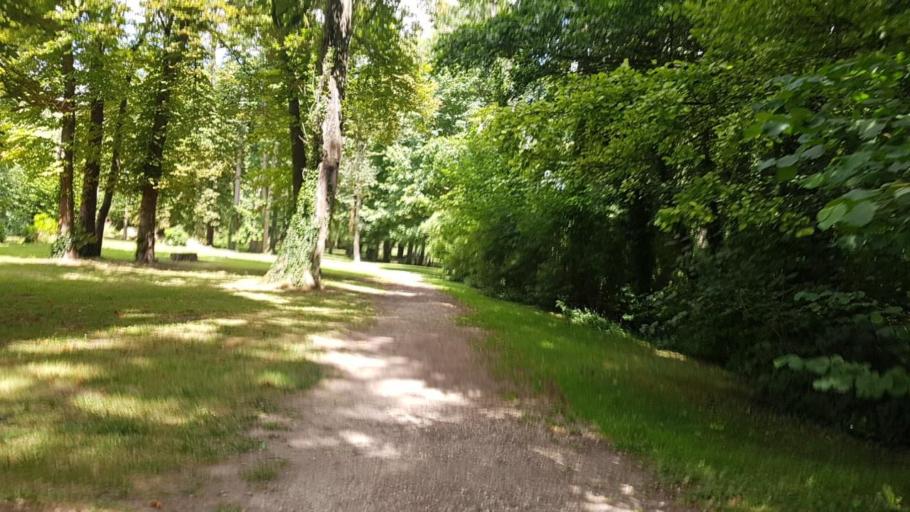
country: FR
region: Ile-de-France
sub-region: Departement de Seine-et-Marne
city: Claye-Souilly
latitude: 48.9612
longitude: 2.6743
